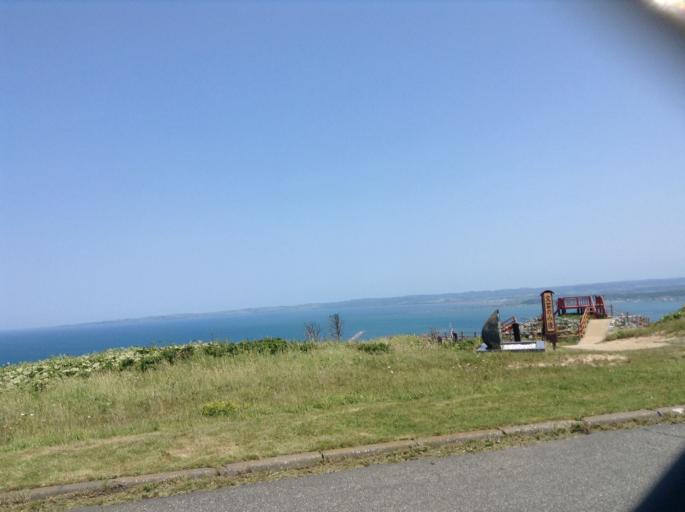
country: JP
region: Hokkaido
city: Wakkanai
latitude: 45.4173
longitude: 141.6636
